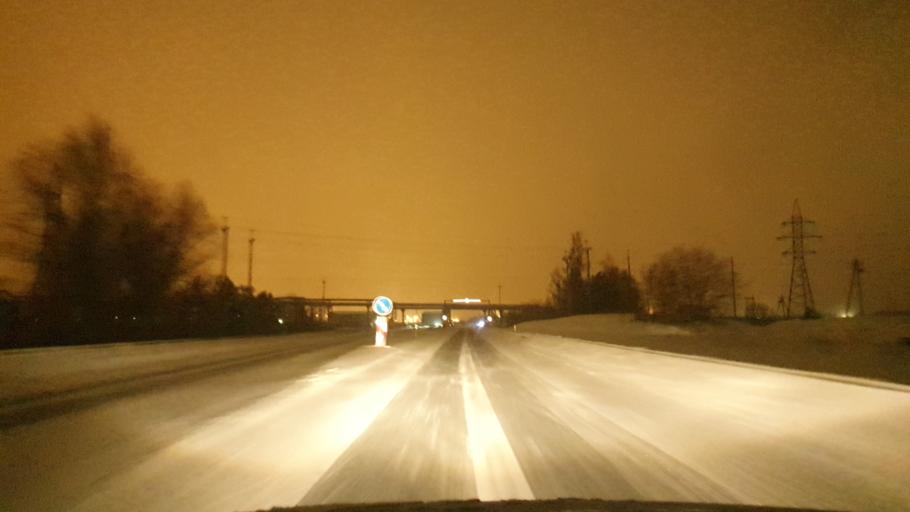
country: EE
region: Harju
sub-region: Joelaehtme vald
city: Loo
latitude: 59.4657
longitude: 24.9801
